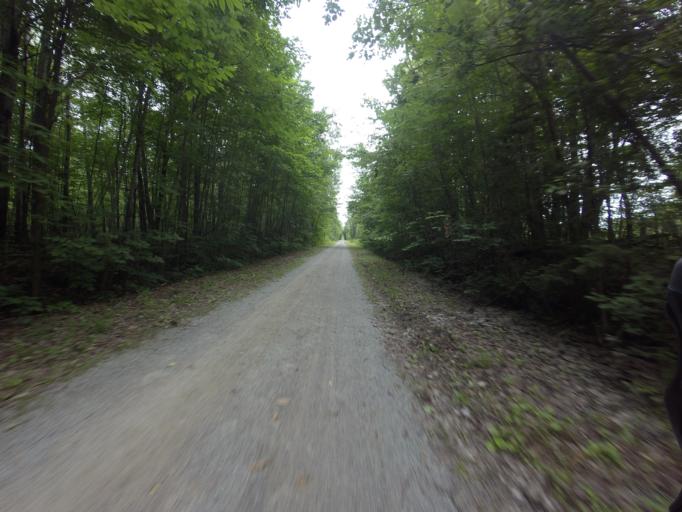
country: CA
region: Ontario
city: Ottawa
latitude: 45.2242
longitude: -75.6210
